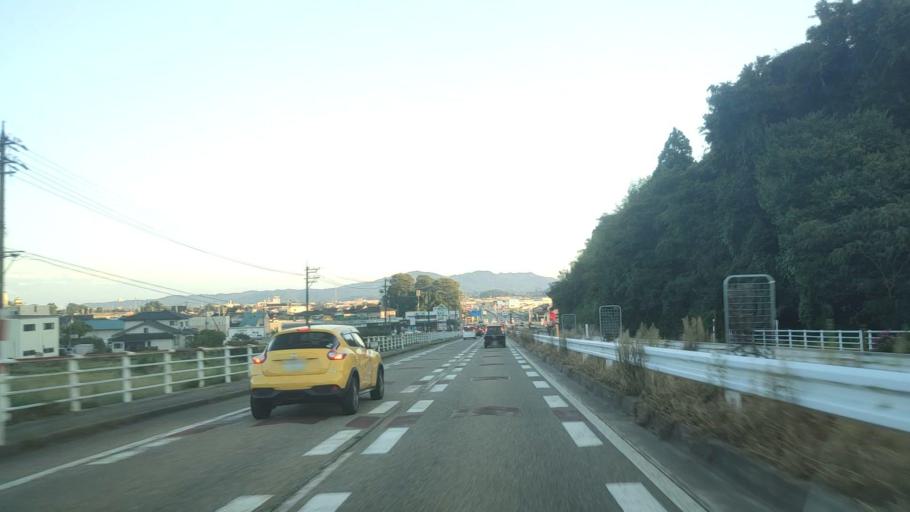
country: JP
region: Toyama
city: Himi
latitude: 36.8478
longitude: 136.9800
